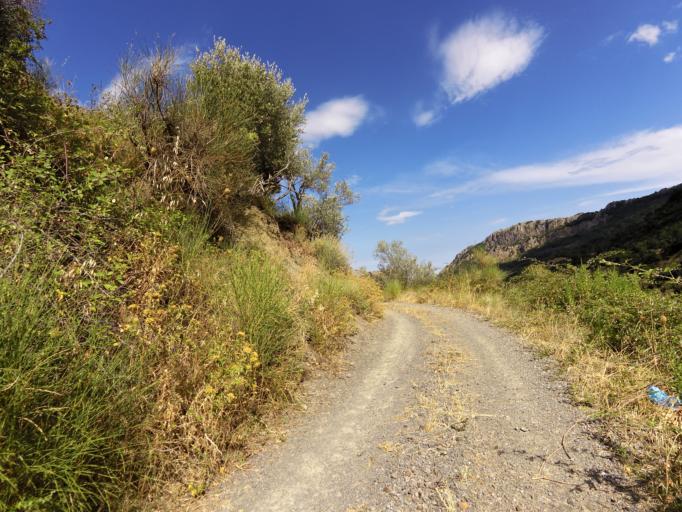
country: IT
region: Calabria
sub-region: Provincia di Reggio Calabria
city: Pazzano
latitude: 38.4735
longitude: 16.4239
